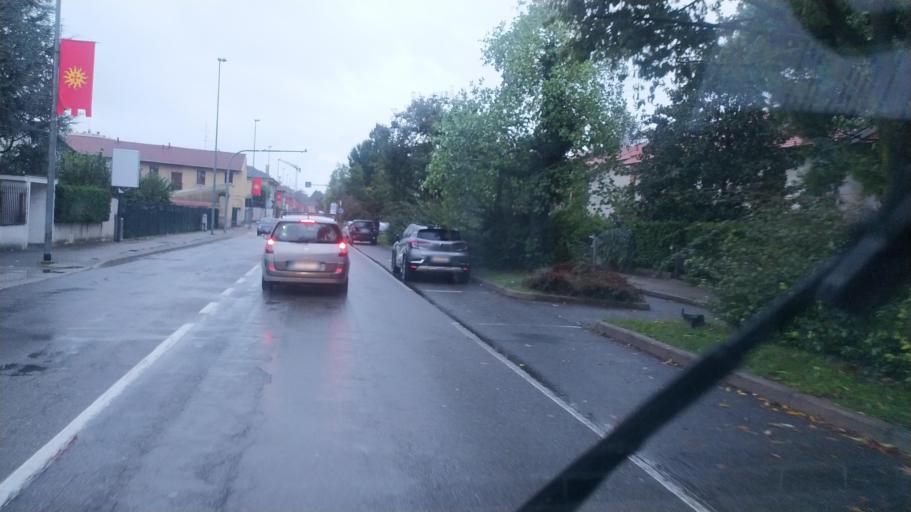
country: IT
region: Lombardy
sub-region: Citta metropolitana di Milano
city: Legnano
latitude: 45.6083
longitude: 8.9268
